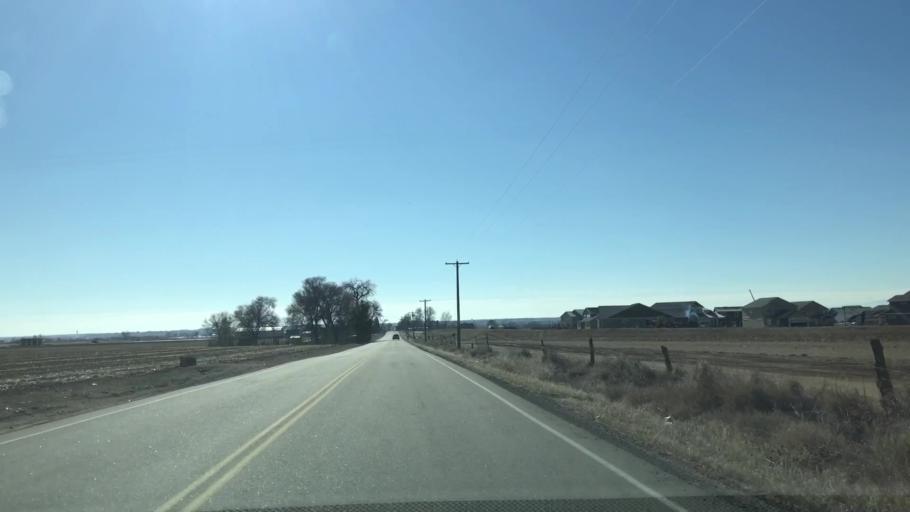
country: US
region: Colorado
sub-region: Weld County
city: Windsor
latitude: 40.5154
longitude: -104.9442
